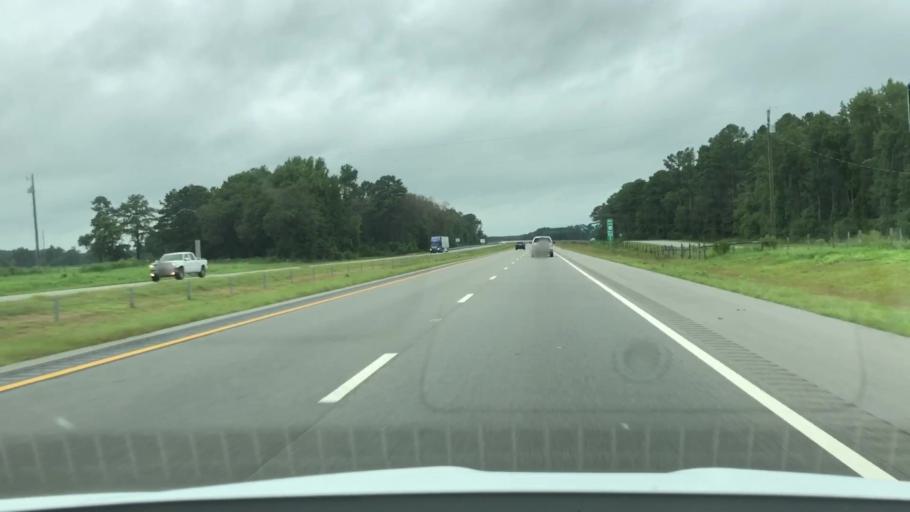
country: US
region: North Carolina
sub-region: Wayne County
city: Elroy
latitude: 35.3476
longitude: -77.8466
